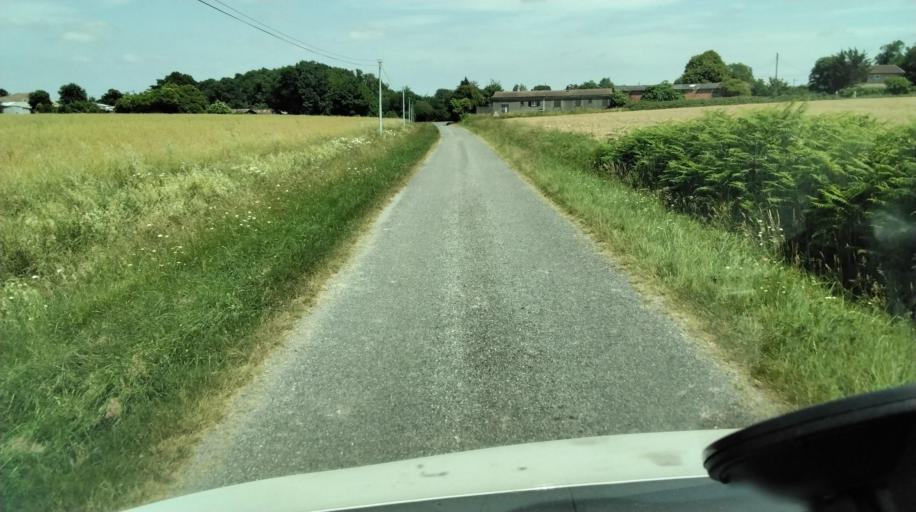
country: FR
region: Midi-Pyrenees
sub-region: Departement de la Haute-Garonne
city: Rieumes
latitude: 43.4007
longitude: 1.1092
